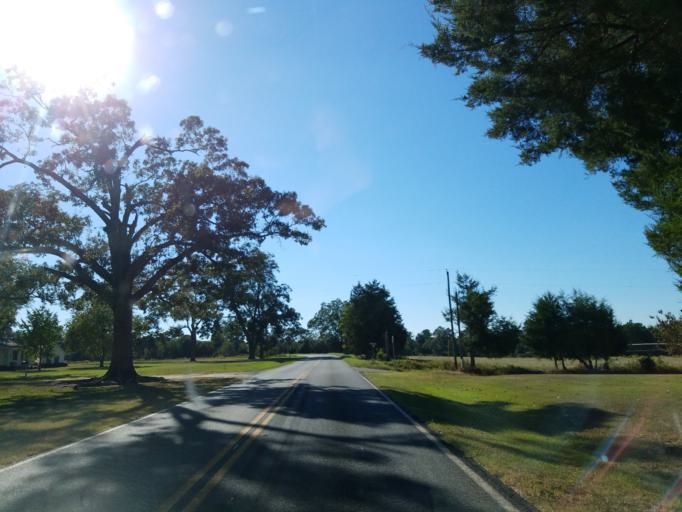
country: US
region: Georgia
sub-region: Dooly County
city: Unadilla
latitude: 32.2526
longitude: -83.7870
